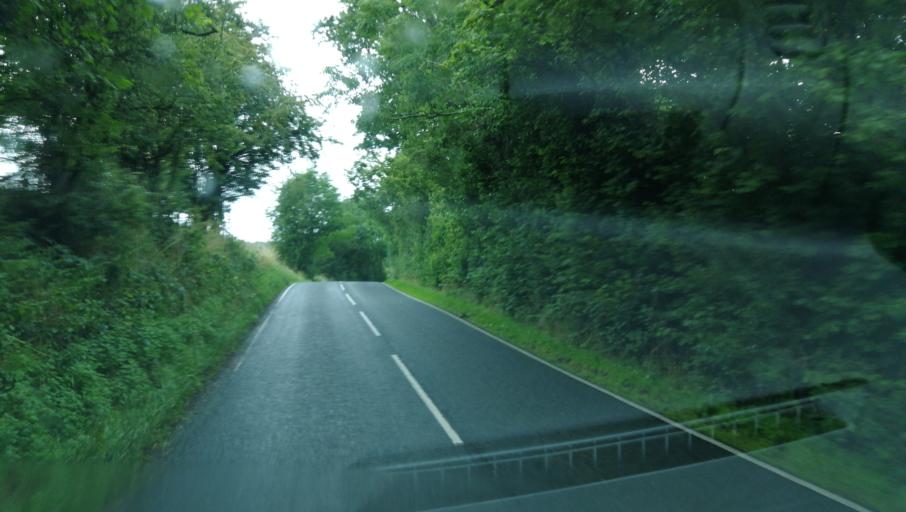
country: GB
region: England
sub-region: Cumbria
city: Penrith
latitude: 54.6270
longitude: -2.8125
